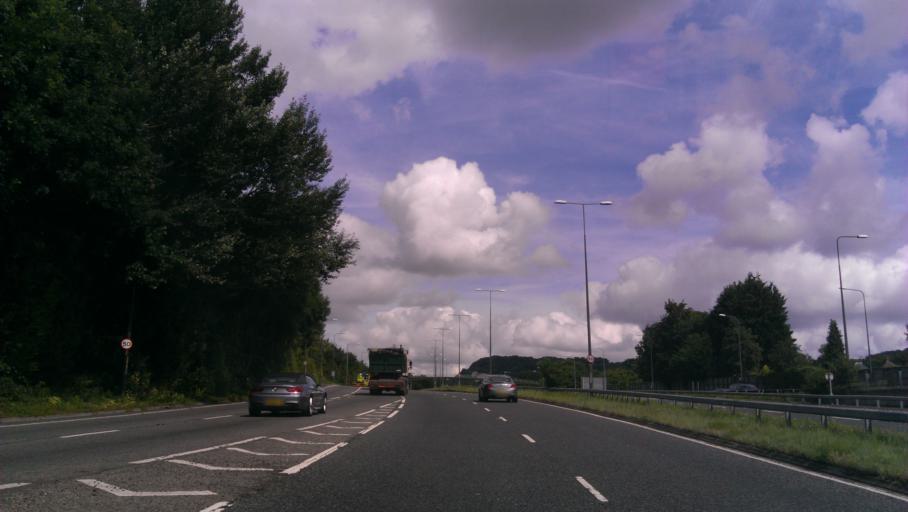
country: GB
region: England
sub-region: Kent
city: Boxley
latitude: 51.3024
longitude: 0.5132
